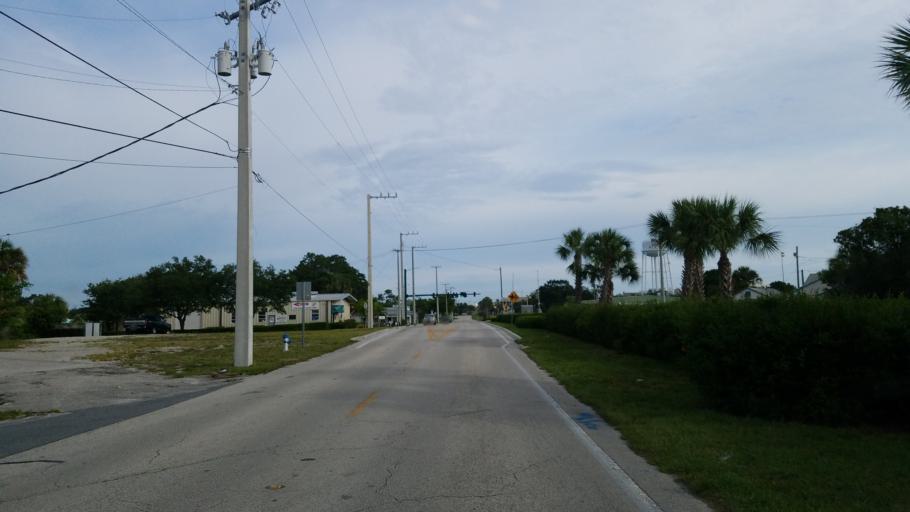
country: US
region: Florida
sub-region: Martin County
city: Stuart
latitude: 27.1928
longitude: -80.2483
